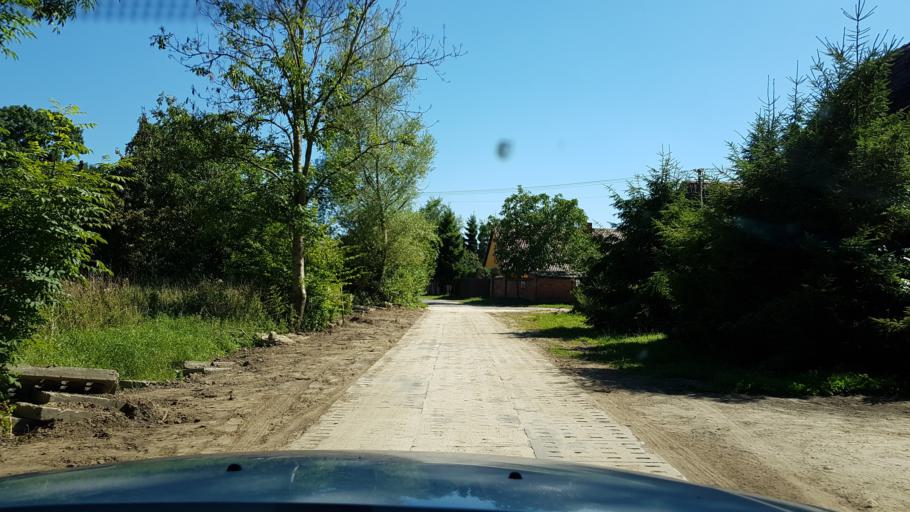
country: PL
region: West Pomeranian Voivodeship
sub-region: Powiat slawienski
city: Darlowo
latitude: 54.4595
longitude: 16.4869
